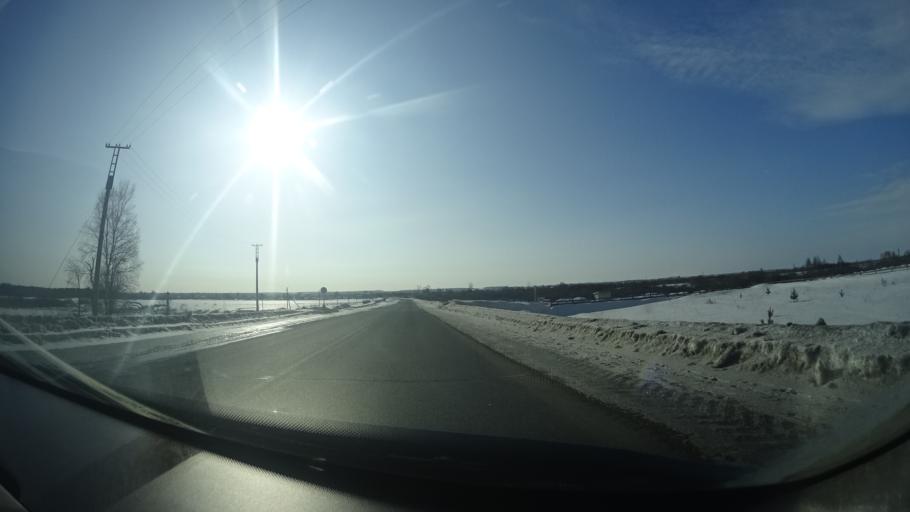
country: RU
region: Perm
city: Kuyeda
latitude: 56.4634
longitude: 55.5940
